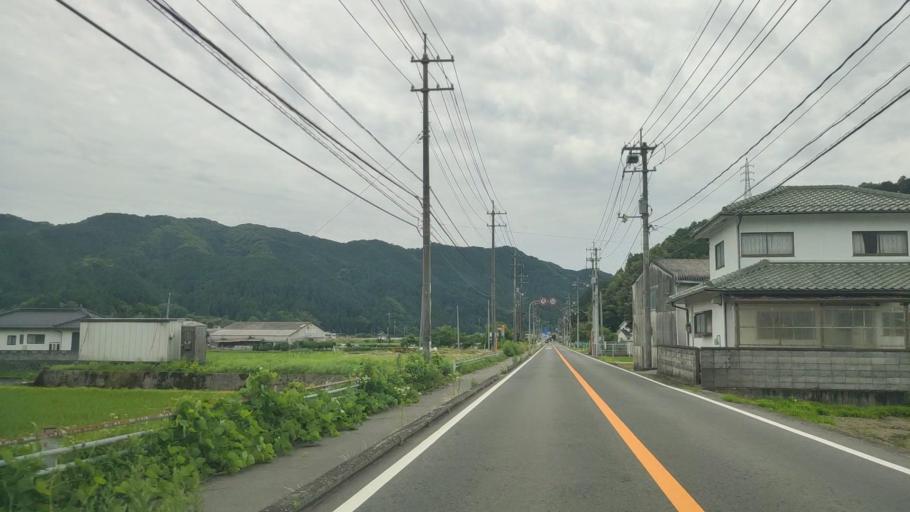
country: JP
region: Hyogo
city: Yamazakicho-nakabirose
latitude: 35.1011
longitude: 134.3244
